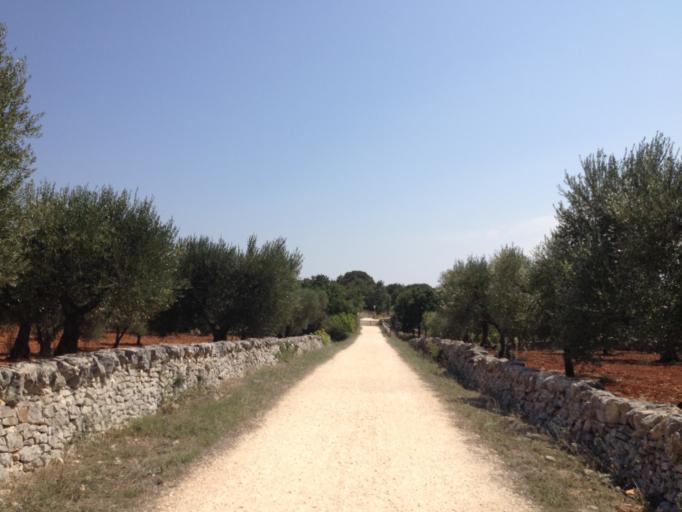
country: IT
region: Apulia
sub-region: Provincia di Brindisi
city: Cisternino
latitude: 40.7099
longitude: 17.4107
